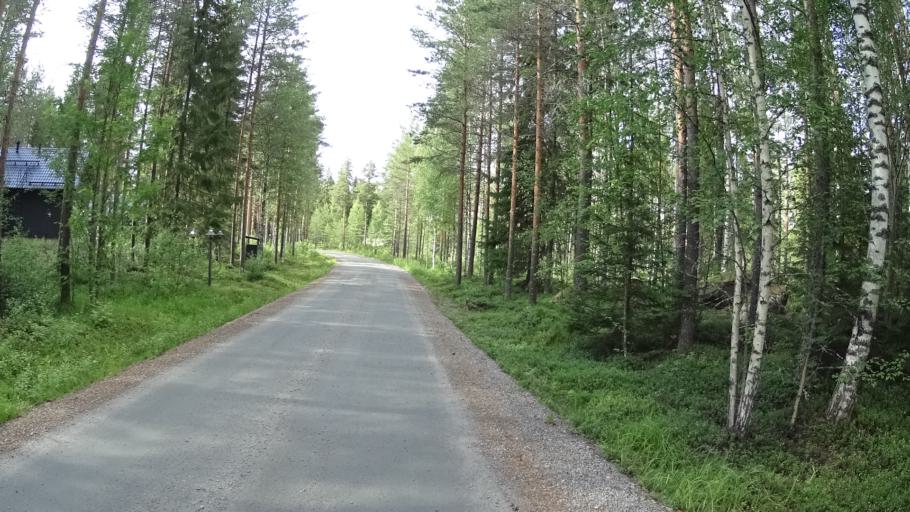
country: FI
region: Southern Ostrobothnia
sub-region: Kuusiokunnat
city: AEhtaeri
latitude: 62.5261
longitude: 24.2006
